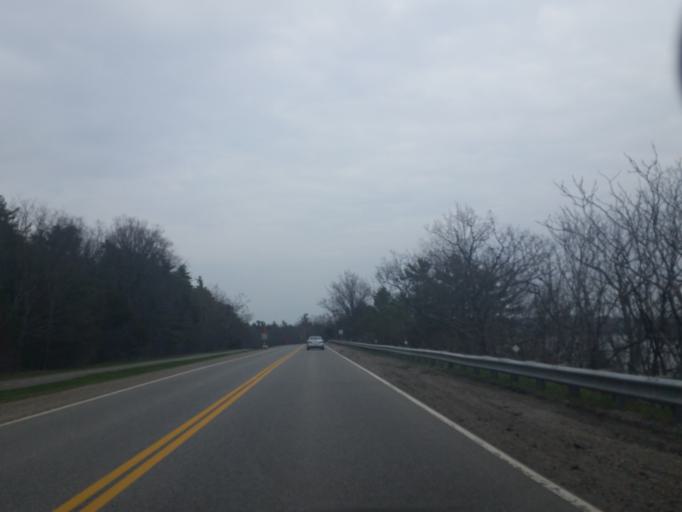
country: US
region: New York
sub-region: Jefferson County
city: Alexandria Bay
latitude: 44.3688
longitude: -75.9674
